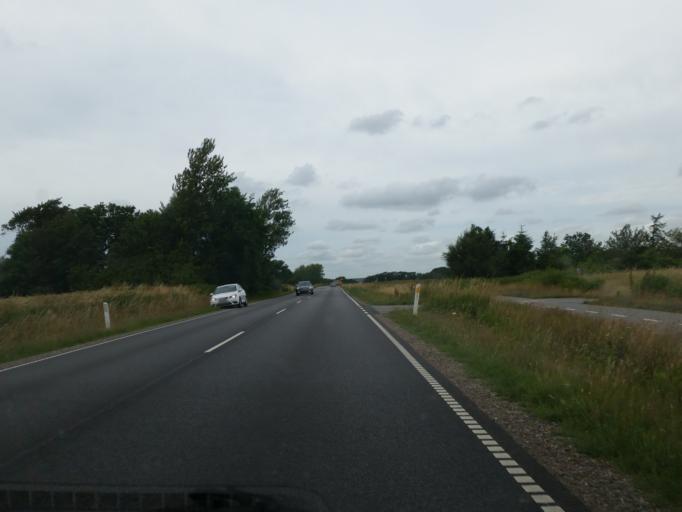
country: DK
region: South Denmark
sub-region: Esbjerg Kommune
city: Ribe
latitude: 55.2594
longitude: 8.7224
